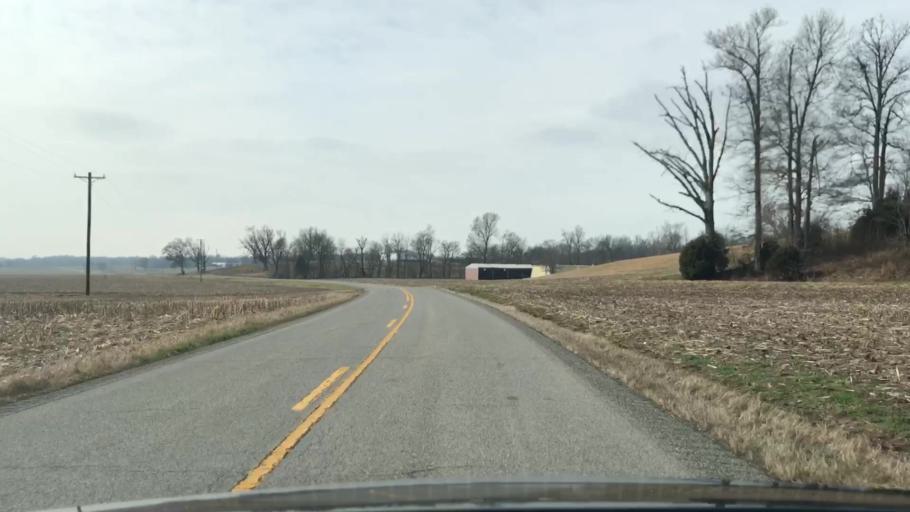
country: US
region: Kentucky
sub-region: Webster County
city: Sebree
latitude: 37.5145
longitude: -87.4115
